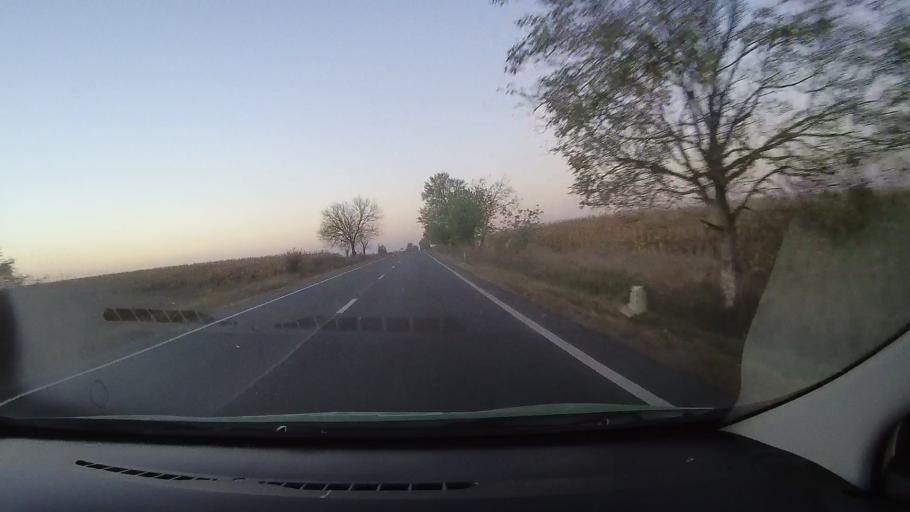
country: RO
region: Bihor
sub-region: Comuna Tarcea
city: Tarcea
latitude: 47.4716
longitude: 22.1650
